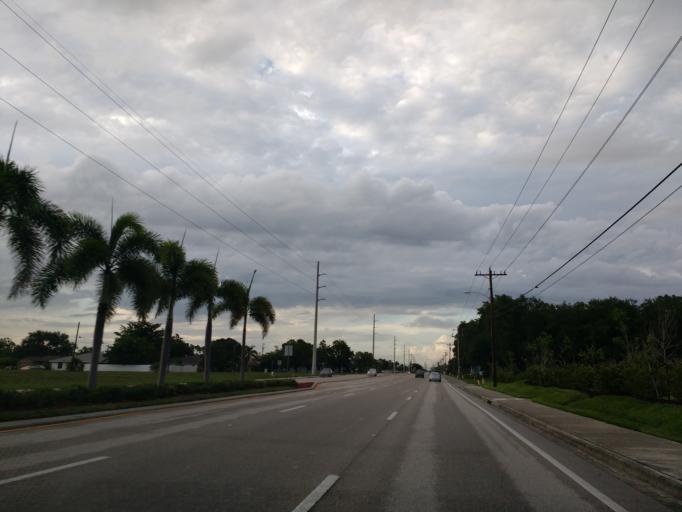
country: US
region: Florida
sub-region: Lee County
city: Lochmoor Waterway Estates
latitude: 26.6258
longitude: -81.9741
